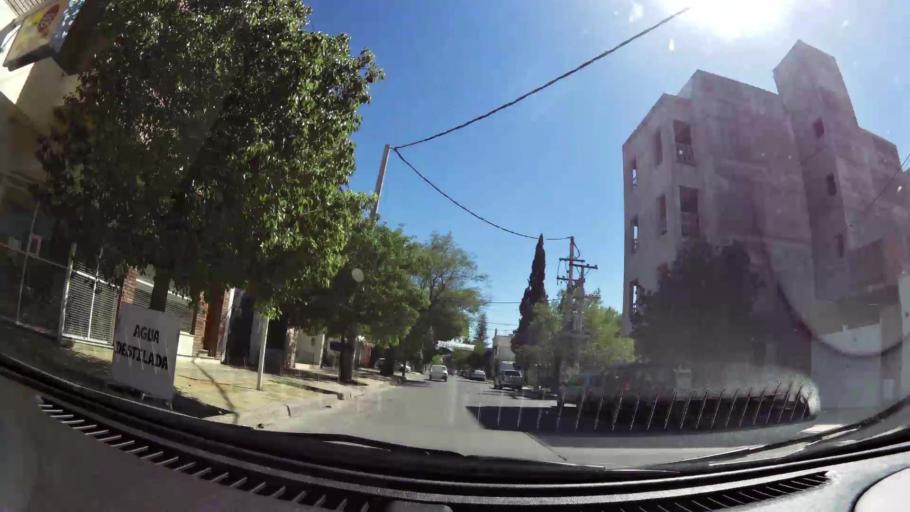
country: AR
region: San Juan
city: San Juan
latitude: -31.5466
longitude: -68.5234
